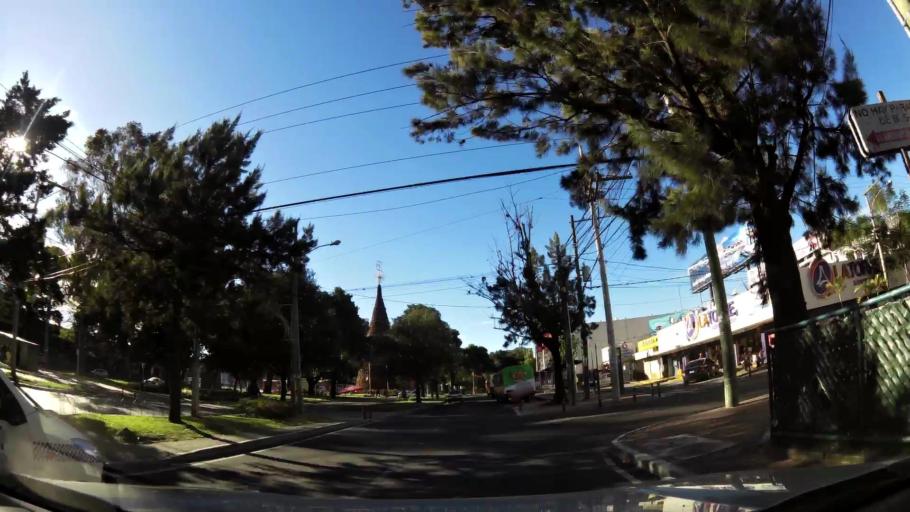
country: GT
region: Guatemala
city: Santa Catarina Pinula
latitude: 14.5960
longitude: -90.5178
